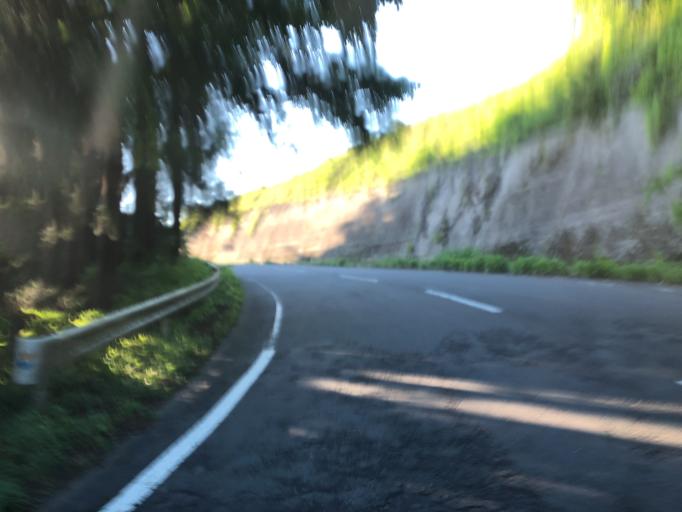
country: JP
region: Fukushima
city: Ishikawa
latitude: 37.0083
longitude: 140.4354
